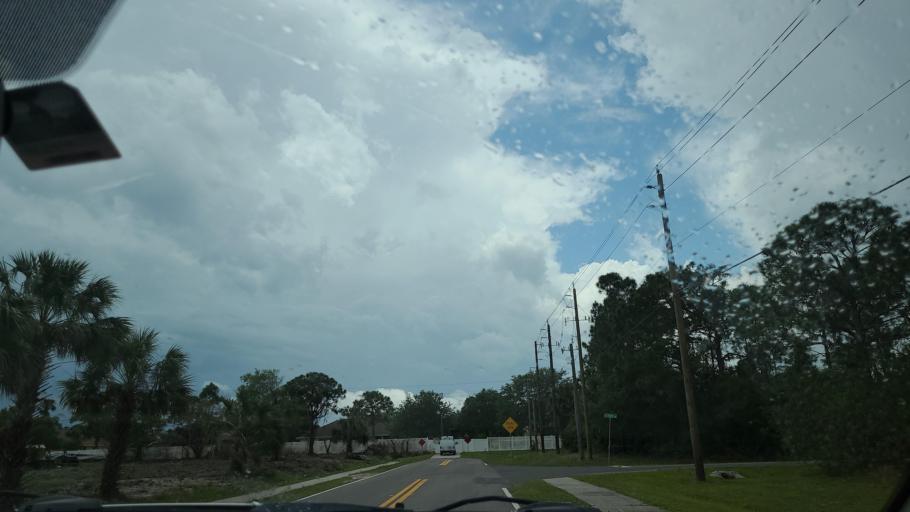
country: US
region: Florida
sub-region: Brevard County
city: Grant-Valkaria
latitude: 27.9458
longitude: -80.6446
